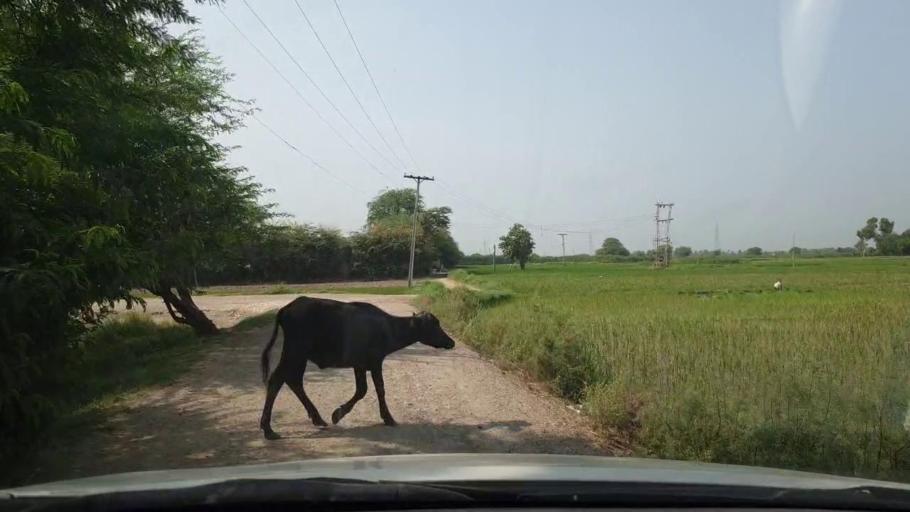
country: PK
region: Sindh
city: Shikarpur
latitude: 27.9821
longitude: 68.6723
